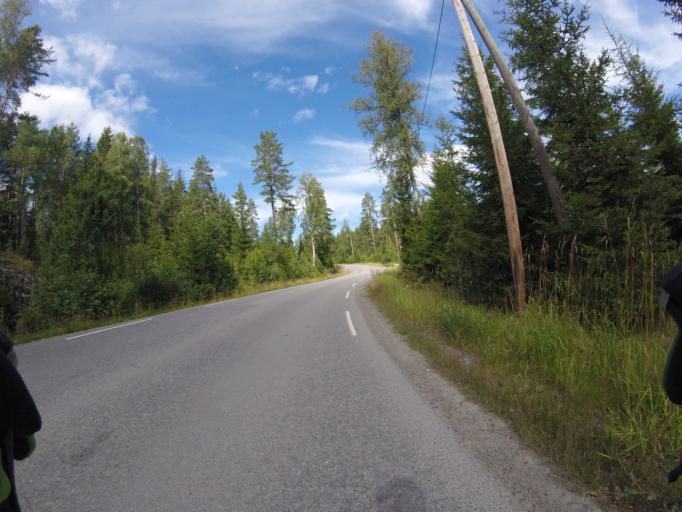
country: NO
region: Akershus
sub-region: Lorenskog
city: Kjenn
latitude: 59.8932
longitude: 10.9753
